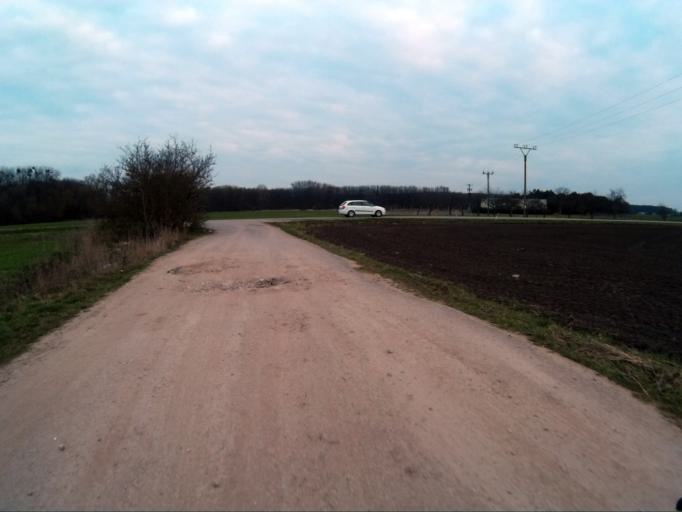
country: CZ
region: South Moravian
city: Velke Nemcice
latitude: 48.9837
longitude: 16.6398
